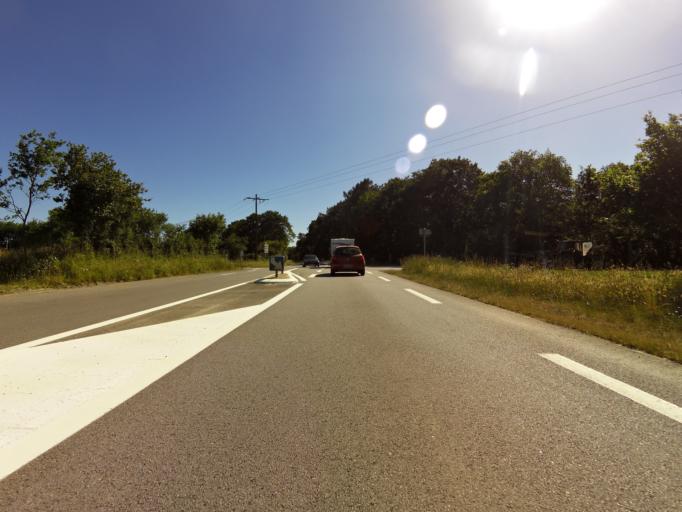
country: FR
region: Brittany
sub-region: Departement du Morbihan
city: Ferel
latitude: 47.5115
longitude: -2.3755
